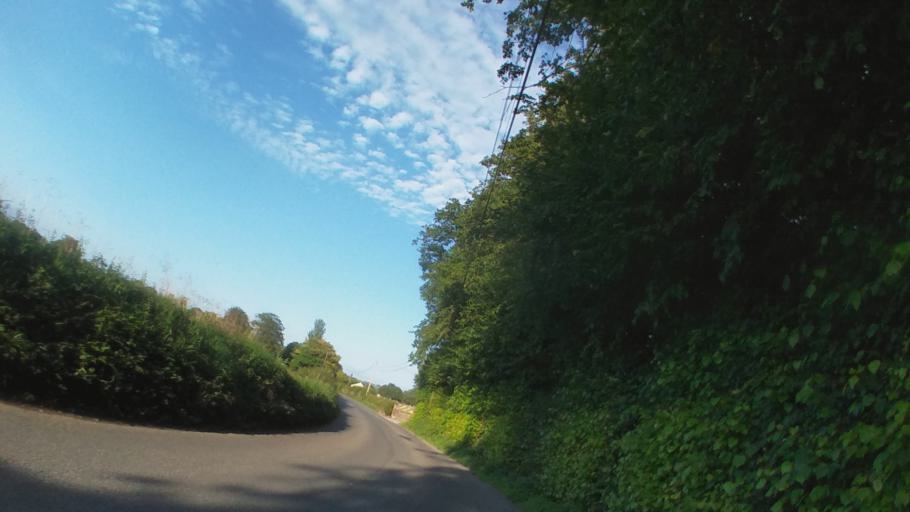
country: IE
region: Leinster
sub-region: Kilkenny
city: Kilkenny
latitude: 52.6756
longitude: -7.1951
